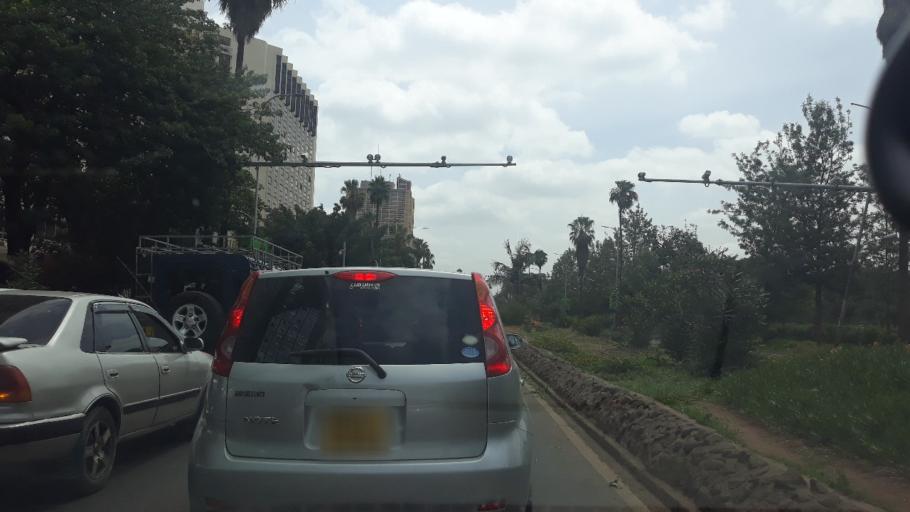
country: KE
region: Nairobi Area
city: Nairobi
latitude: -1.2832
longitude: 36.8158
